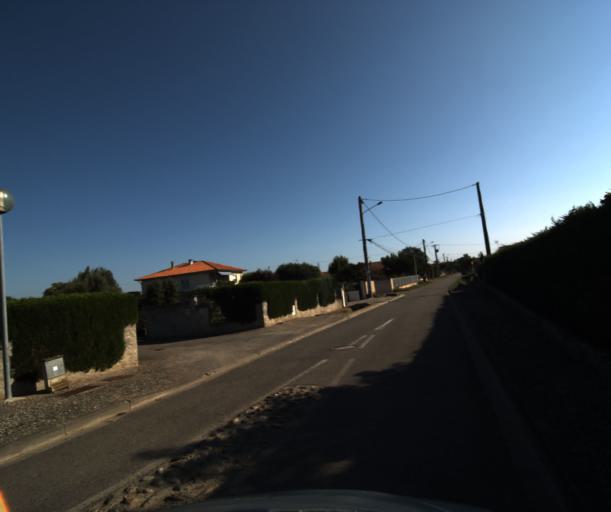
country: FR
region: Midi-Pyrenees
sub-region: Departement de la Haute-Garonne
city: Eaunes
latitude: 43.4352
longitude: 1.3653
